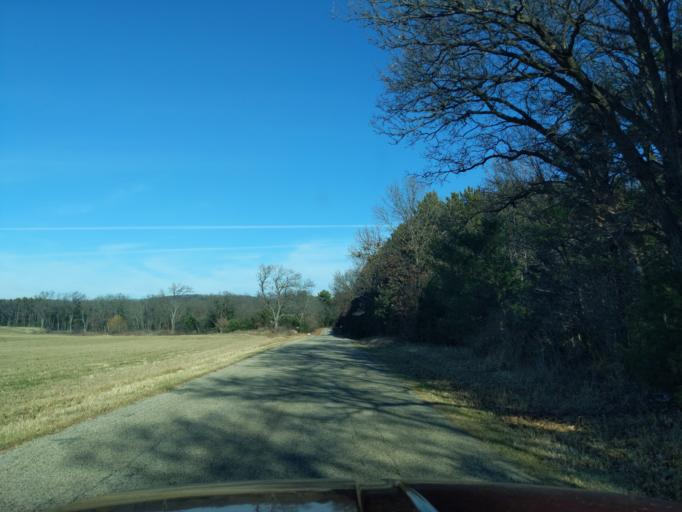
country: US
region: Wisconsin
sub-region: Waushara County
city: Silver Lake
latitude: 44.1021
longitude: -89.1789
